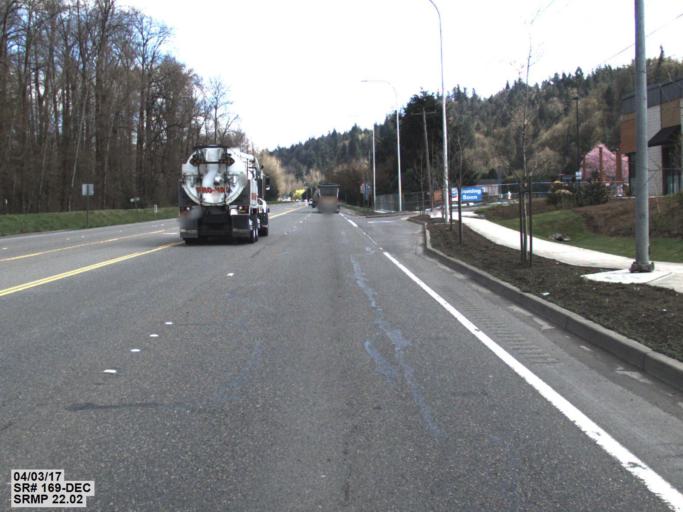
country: US
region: Washington
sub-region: King County
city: Fairwood
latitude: 47.4651
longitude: -122.1363
